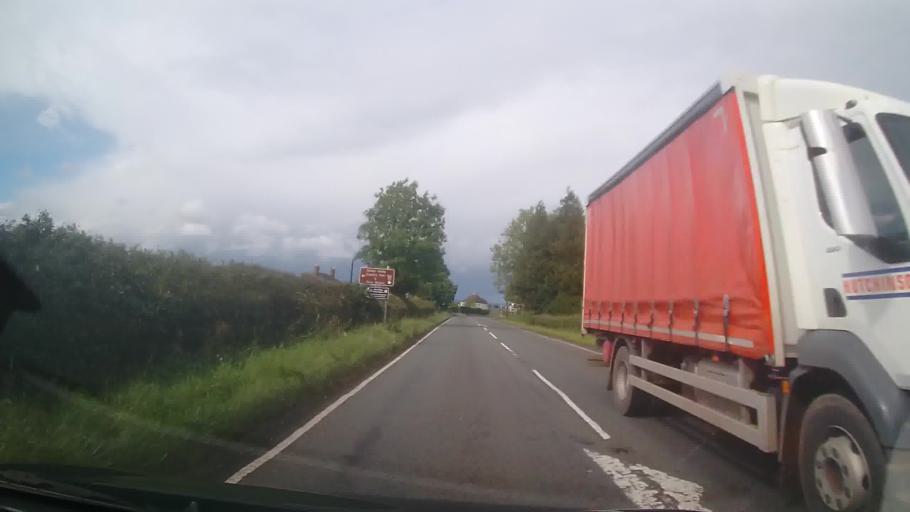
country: GB
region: England
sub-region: Shropshire
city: Romsley
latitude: 52.4461
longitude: -2.3357
